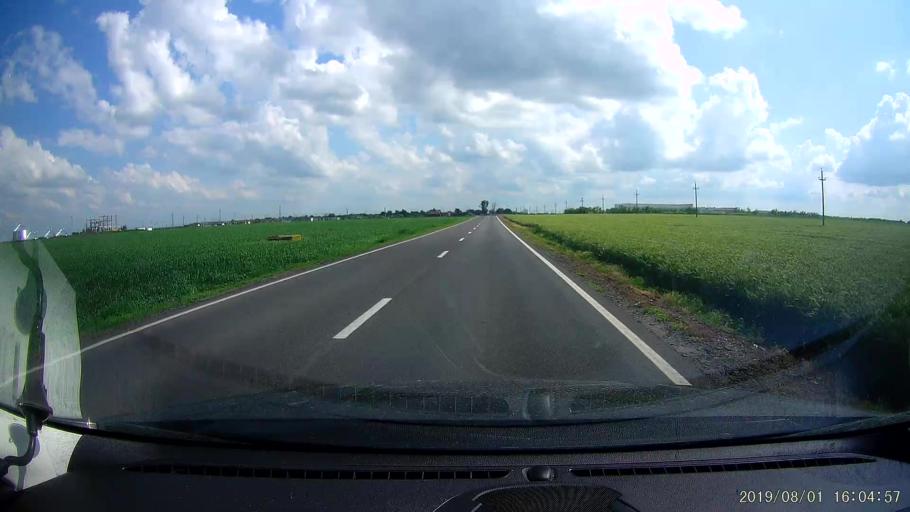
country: RO
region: Calarasi
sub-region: Comuna Dragalina
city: Drajna Noua
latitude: 44.4347
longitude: 27.3779
